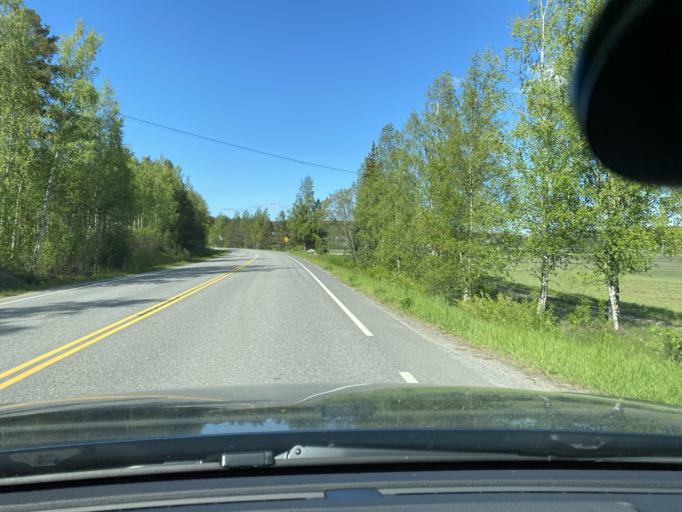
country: FI
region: Varsinais-Suomi
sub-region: Turku
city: Sauvo
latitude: 60.3632
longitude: 22.6729
